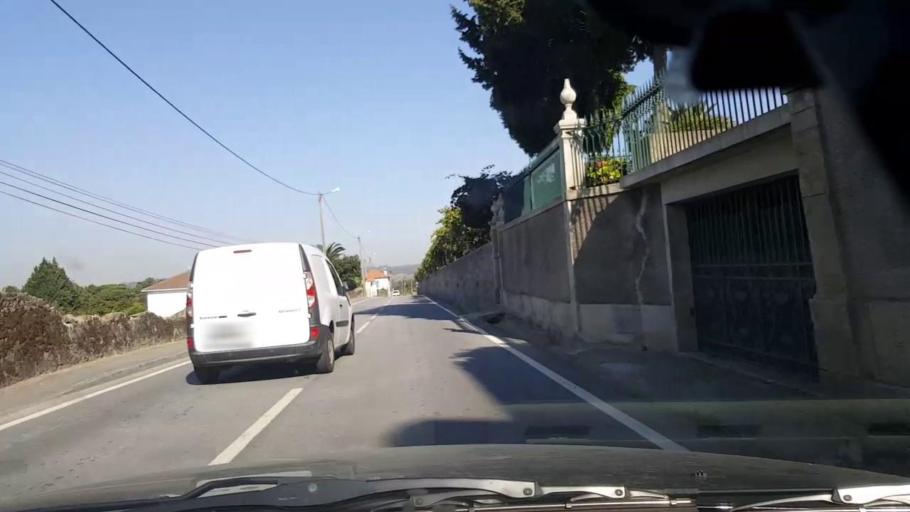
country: PT
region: Porto
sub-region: Vila do Conde
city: Arvore
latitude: 41.3723
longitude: -8.6692
